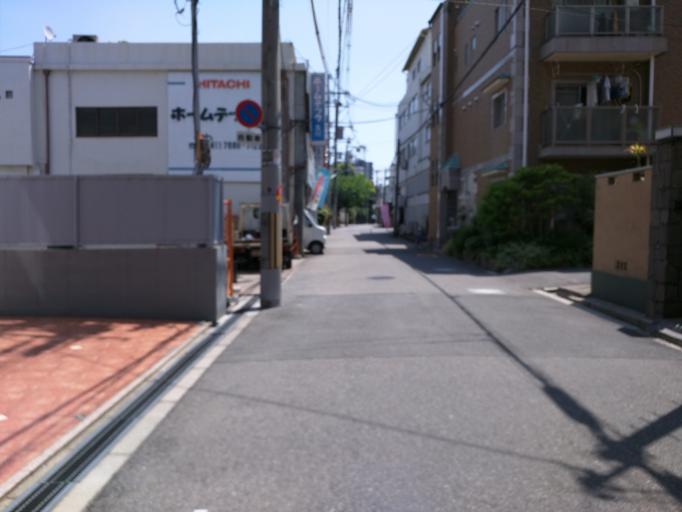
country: JP
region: Osaka
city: Osaka-shi
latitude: 34.6885
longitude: 135.4776
